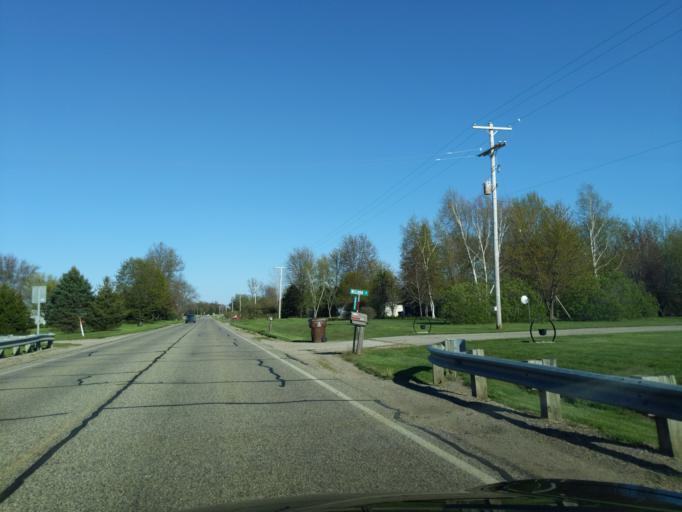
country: US
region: Michigan
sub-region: Ionia County
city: Portland
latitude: 42.8808
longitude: -84.9794
